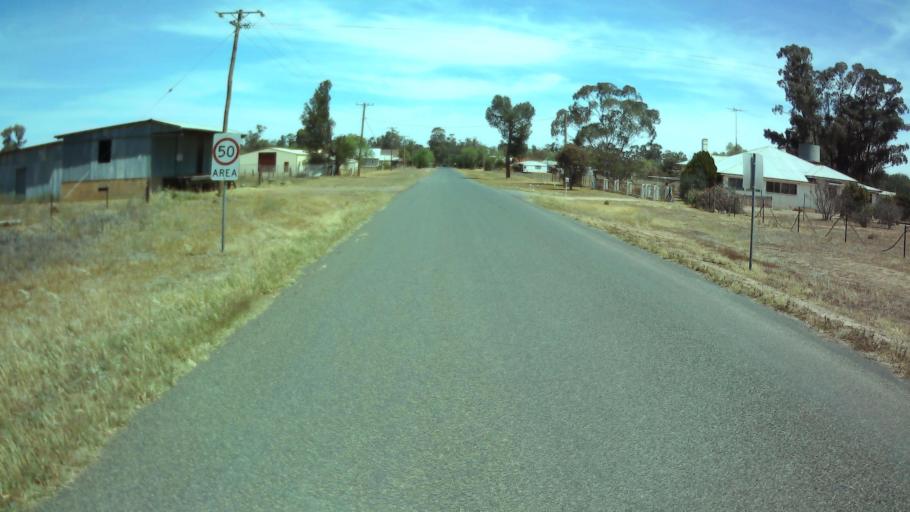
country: AU
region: New South Wales
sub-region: Weddin
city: Grenfell
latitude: -33.8399
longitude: 147.7445
